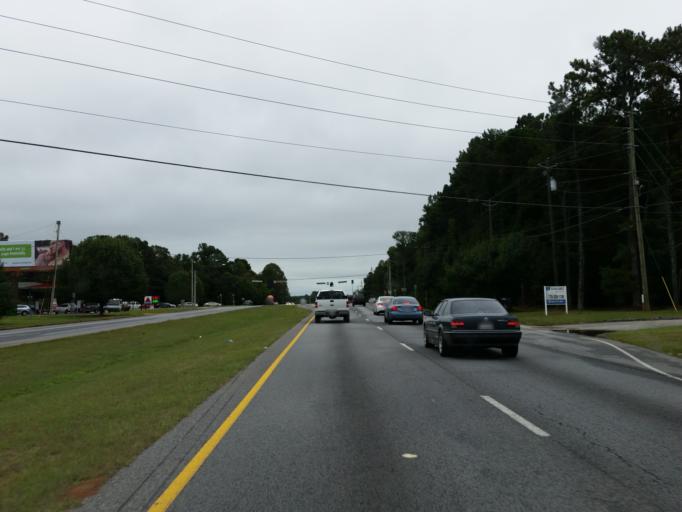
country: US
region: Georgia
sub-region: Clayton County
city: Bonanza
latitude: 33.4830
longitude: -84.3396
